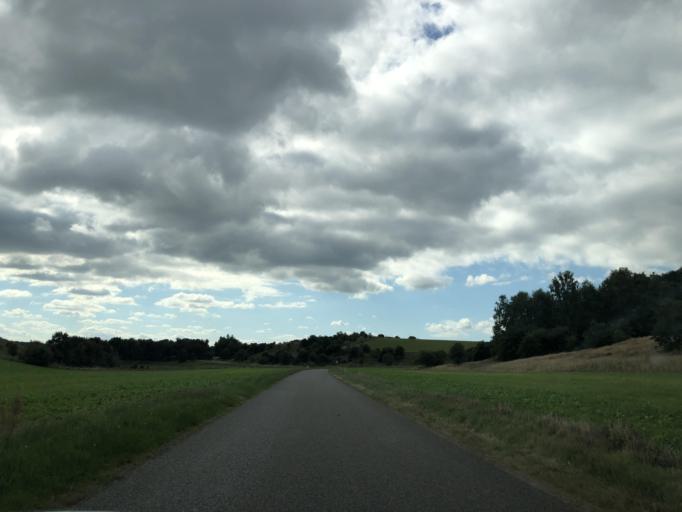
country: DK
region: Central Jutland
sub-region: Viborg Kommune
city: Viborg
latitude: 56.5863
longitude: 9.3990
